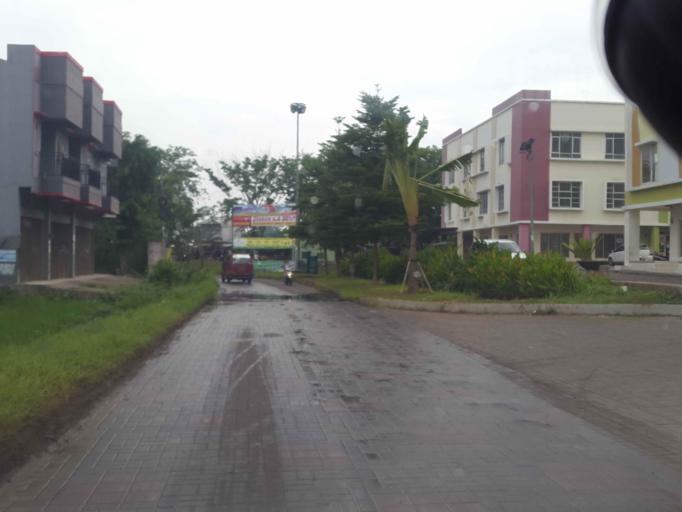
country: ID
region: West Java
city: Cikarang
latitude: -6.2780
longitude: 107.1787
